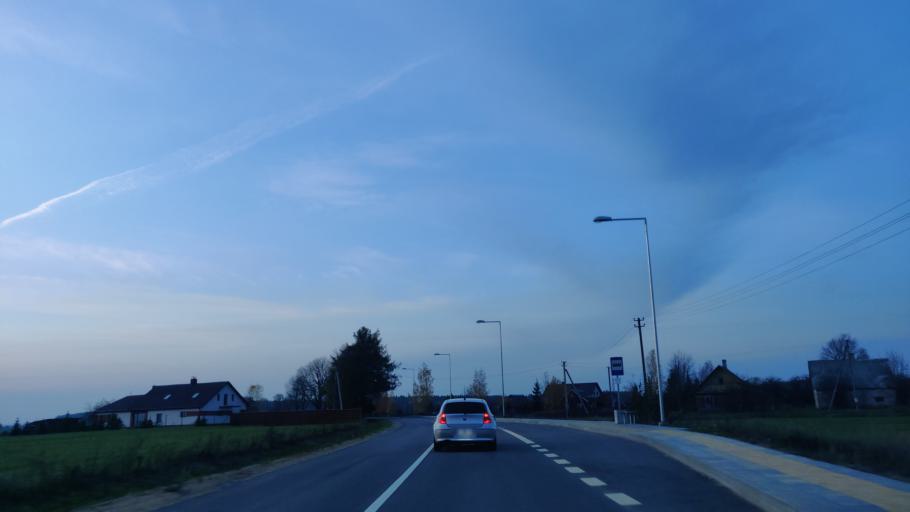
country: LT
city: Lentvaris
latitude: 54.5907
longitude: 25.0488
